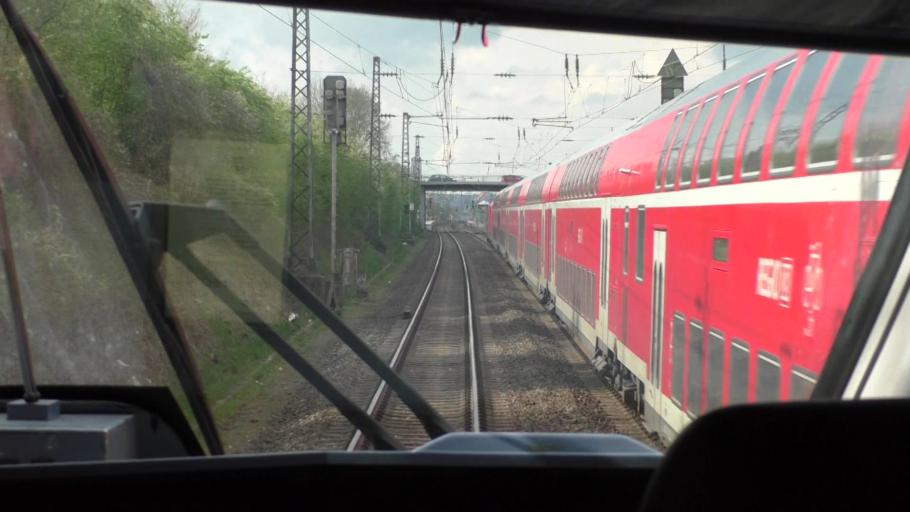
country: DE
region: North Rhine-Westphalia
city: Wesseling
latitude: 50.7920
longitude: 6.9626
